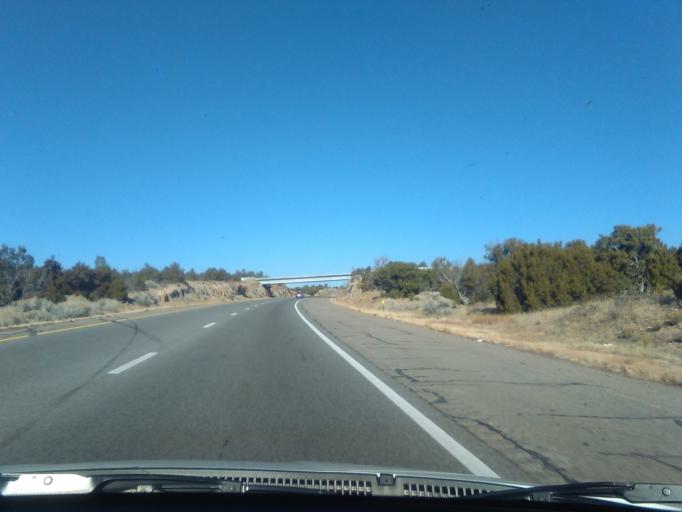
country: US
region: New Mexico
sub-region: Santa Fe County
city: Eldorado at Santa Fe
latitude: 35.5785
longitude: -105.8973
